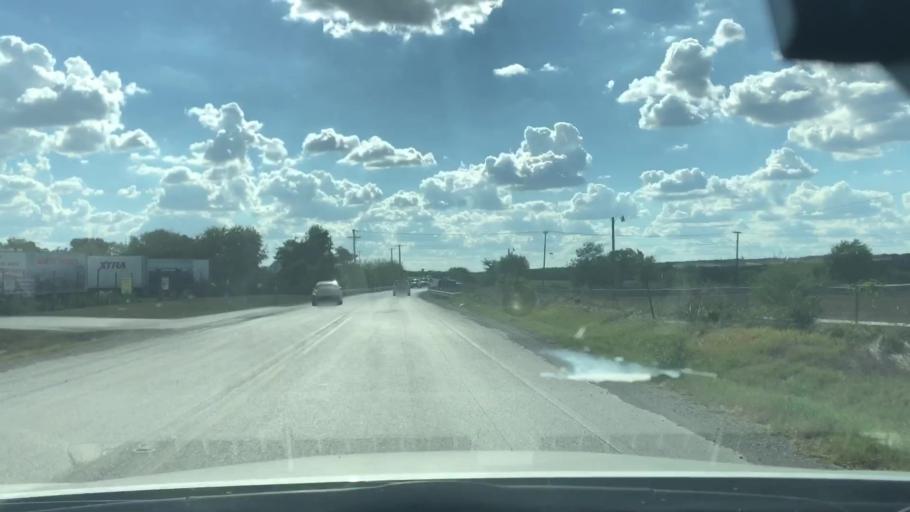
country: US
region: Texas
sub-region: Guadalupe County
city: Northcliff
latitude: 29.6617
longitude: -98.1884
